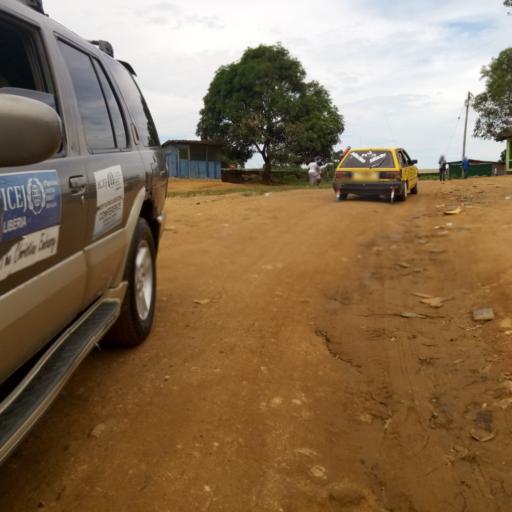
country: LR
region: Montserrado
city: Monrovia
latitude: 6.2969
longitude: -10.7012
